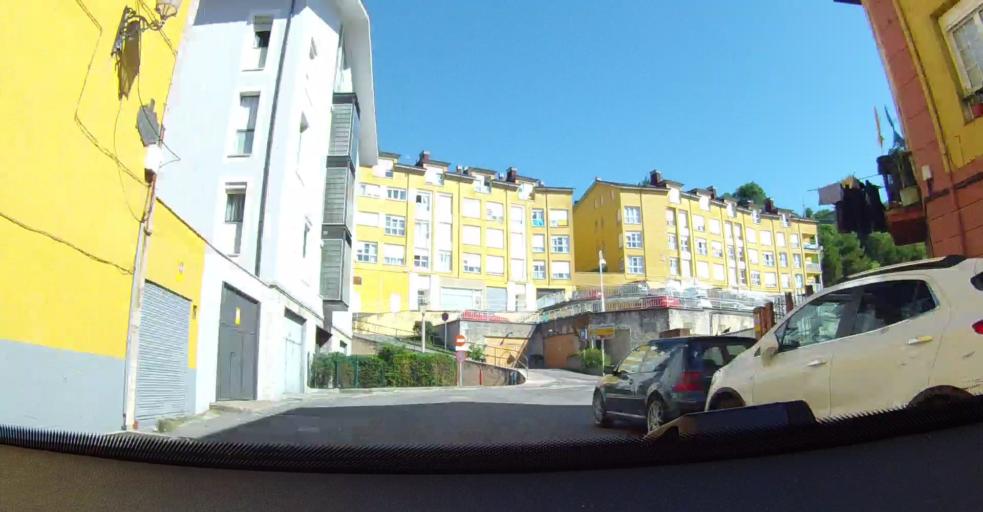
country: ES
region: Asturias
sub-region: Province of Asturias
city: Ribadesella
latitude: 43.4630
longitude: -5.0565
